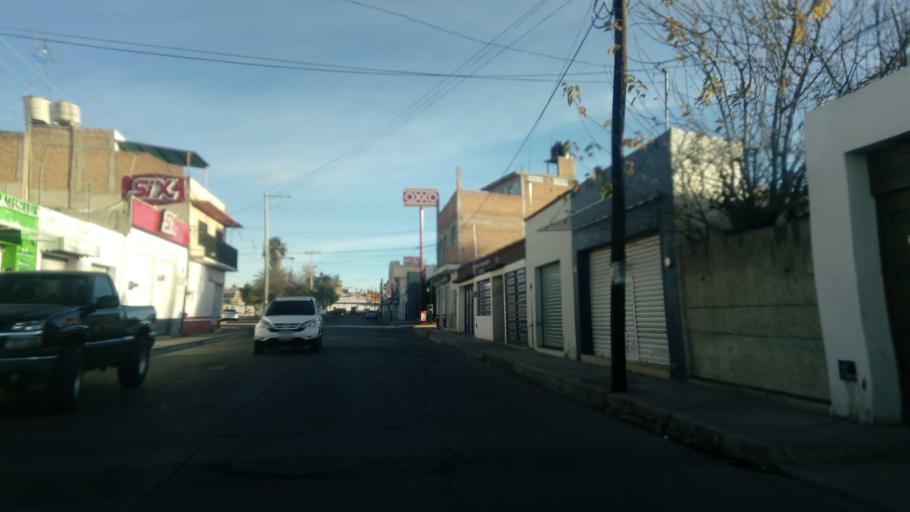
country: MX
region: Durango
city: Victoria de Durango
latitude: 24.0101
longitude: -104.6755
